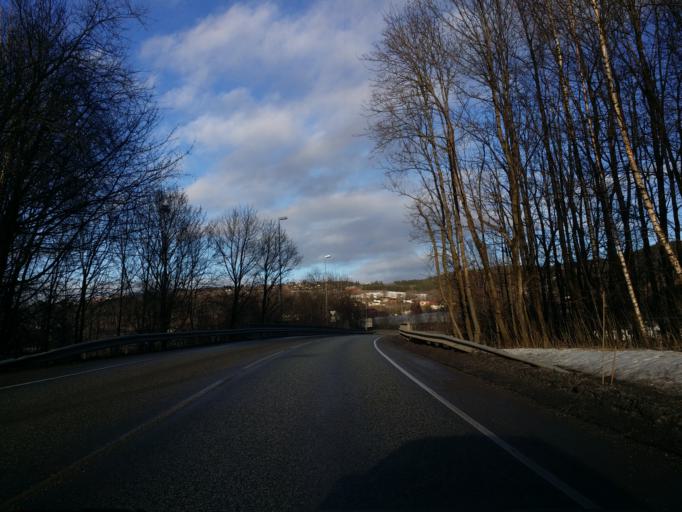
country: NO
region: Buskerud
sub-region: Lier
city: Lierbyen
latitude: 59.7883
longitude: 10.2424
